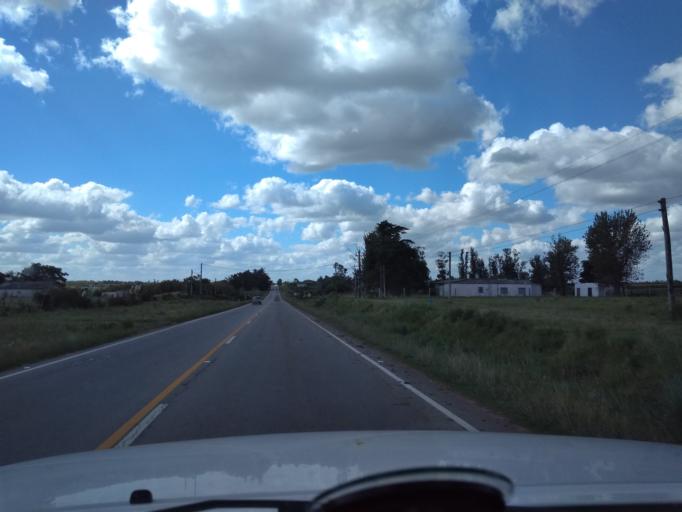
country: UY
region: Canelones
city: Joaquin Suarez
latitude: -34.7014
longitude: -56.0572
